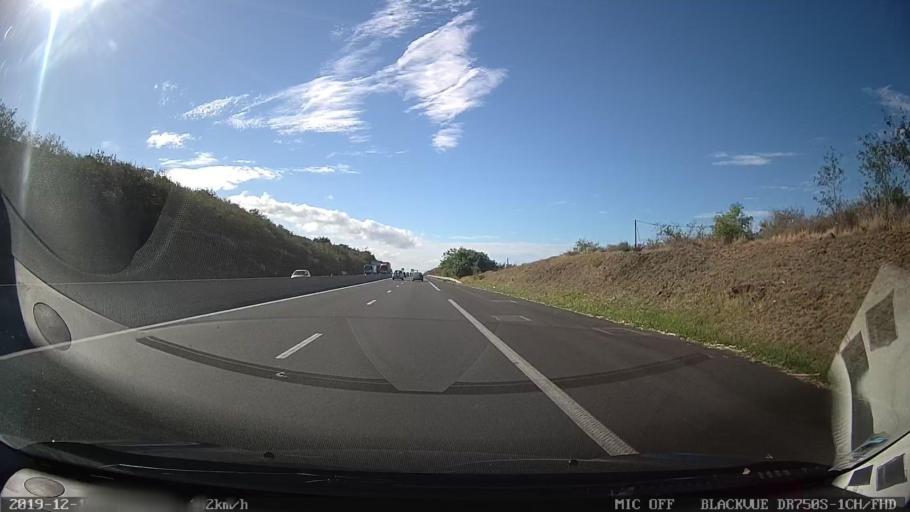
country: RE
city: Piton Saint-Leu
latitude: -21.2094
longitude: 55.2943
